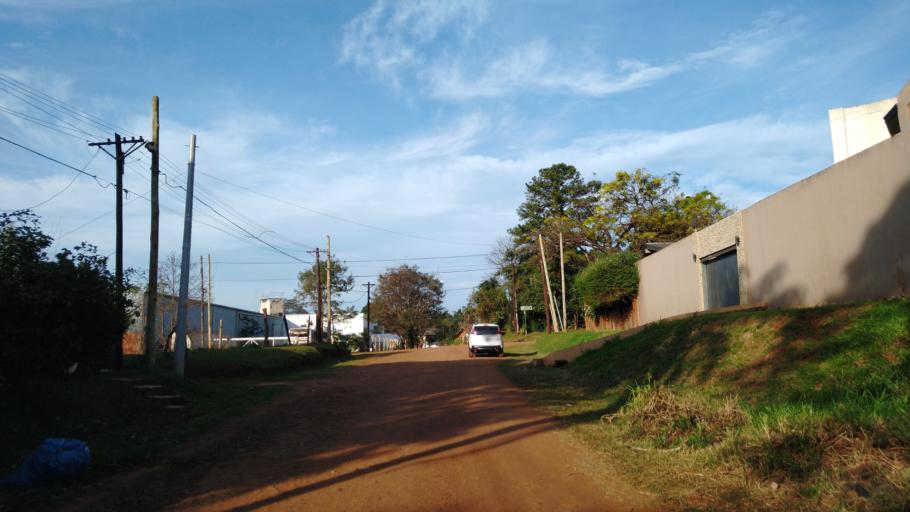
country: AR
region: Misiones
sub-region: Departamento de Capital
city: Posadas
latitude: -27.4005
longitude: -55.9227
